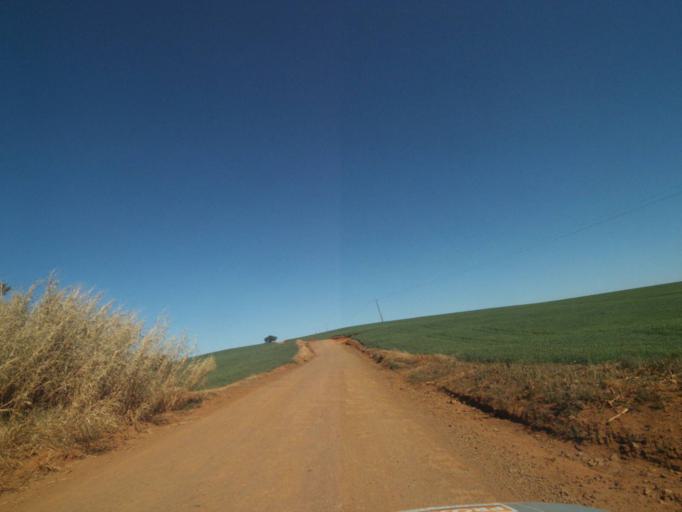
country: BR
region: Parana
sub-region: Tibagi
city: Tibagi
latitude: -24.5997
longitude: -50.6027
